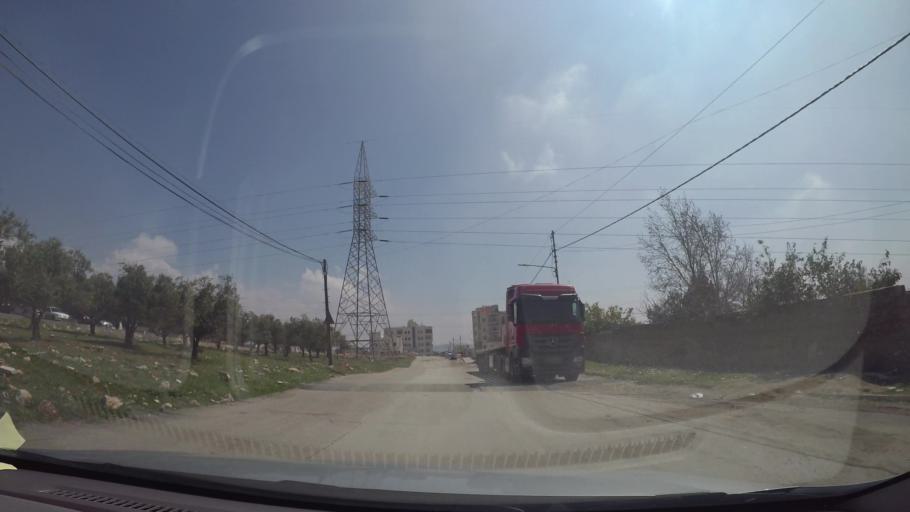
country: JO
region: Amman
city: Al Bunayyat ash Shamaliyah
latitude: 31.8891
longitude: 35.8951
